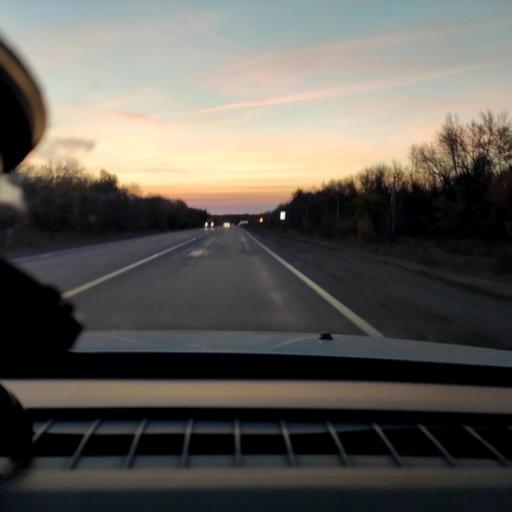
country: RU
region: Samara
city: Novokuybyshevsk
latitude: 52.9862
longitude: 49.8656
